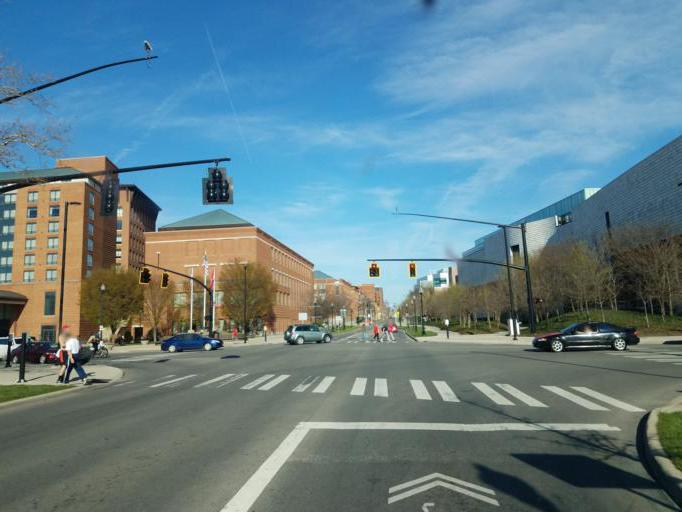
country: US
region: Ohio
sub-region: Franklin County
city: Grandview Heights
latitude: 40.0041
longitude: -83.0179
